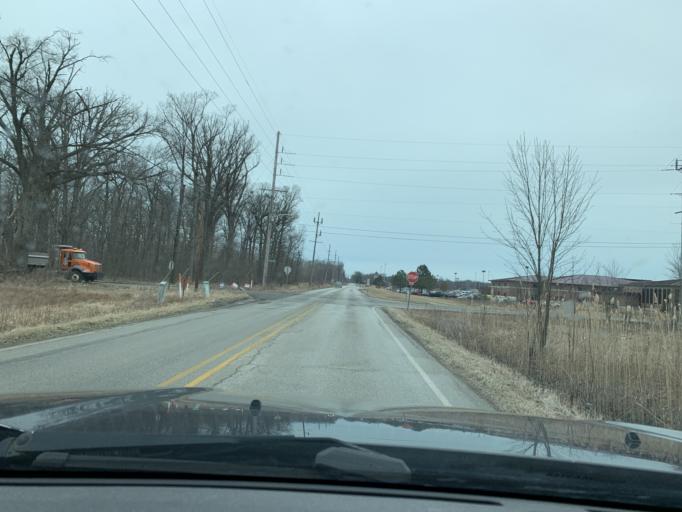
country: US
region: Indiana
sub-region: Porter County
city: Chesterton
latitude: 41.5859
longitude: -87.0667
